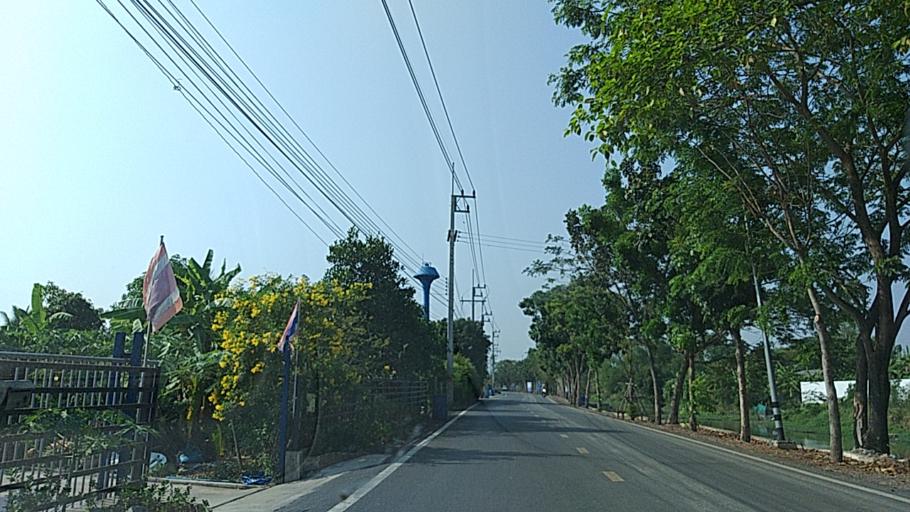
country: TH
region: Pathum Thani
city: Thanyaburi
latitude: 13.9904
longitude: 100.7060
